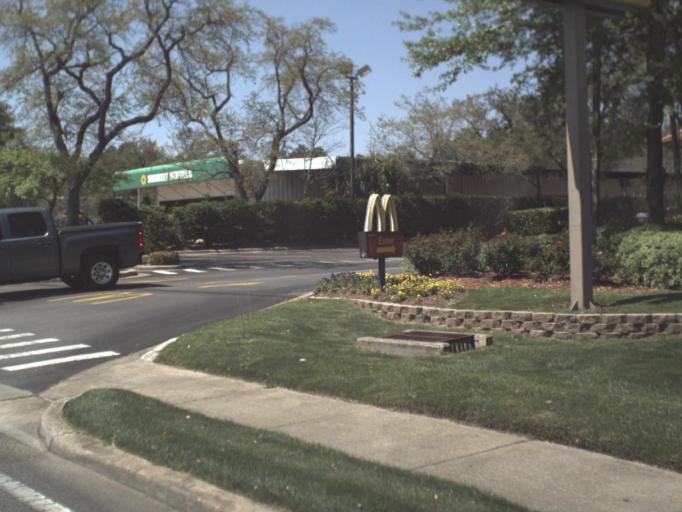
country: US
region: Florida
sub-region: Okaloosa County
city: Niceville
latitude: 30.5166
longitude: -86.4686
